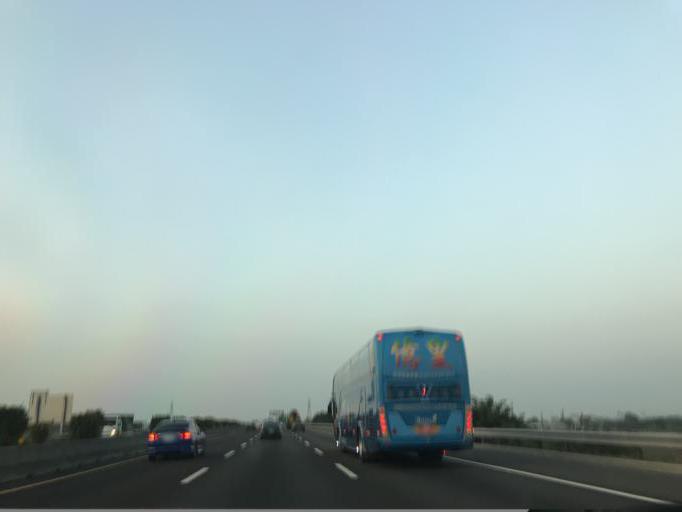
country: TW
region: Taiwan
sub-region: Yunlin
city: Douliu
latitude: 23.7140
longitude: 120.4762
